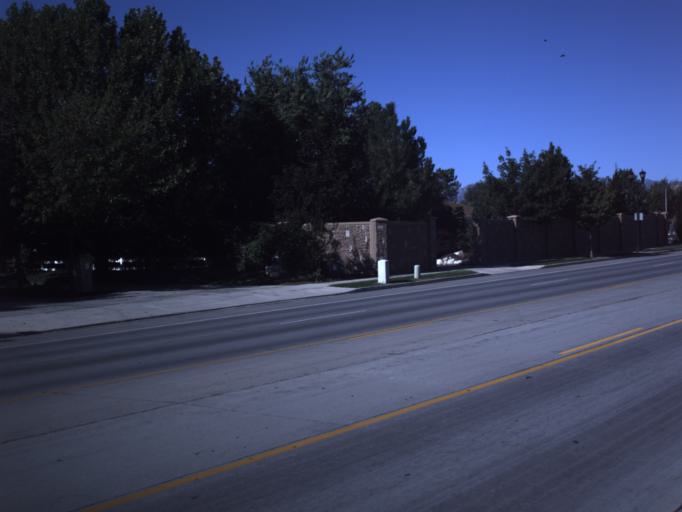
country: US
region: Utah
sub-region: Salt Lake County
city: South Jordan Heights
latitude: 40.5442
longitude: -111.9464
